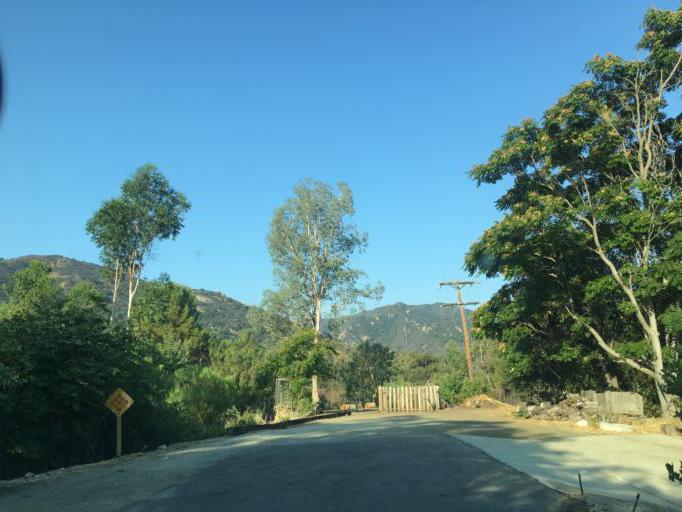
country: US
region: California
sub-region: Los Angeles County
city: Malibu Beach
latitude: 34.0821
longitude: -118.6868
